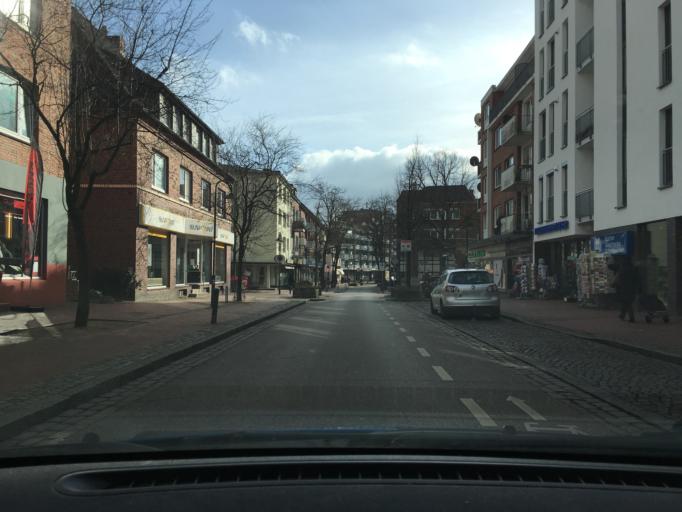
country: DE
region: Schleswig-Holstein
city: Wedel
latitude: 53.5767
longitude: 9.7057
